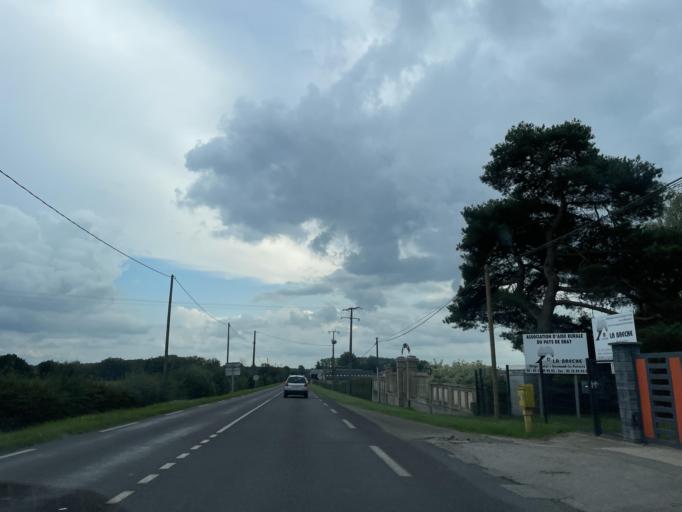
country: FR
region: Haute-Normandie
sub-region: Departement de la Seine-Maritime
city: Cayenne
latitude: 49.5708
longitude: 1.6099
